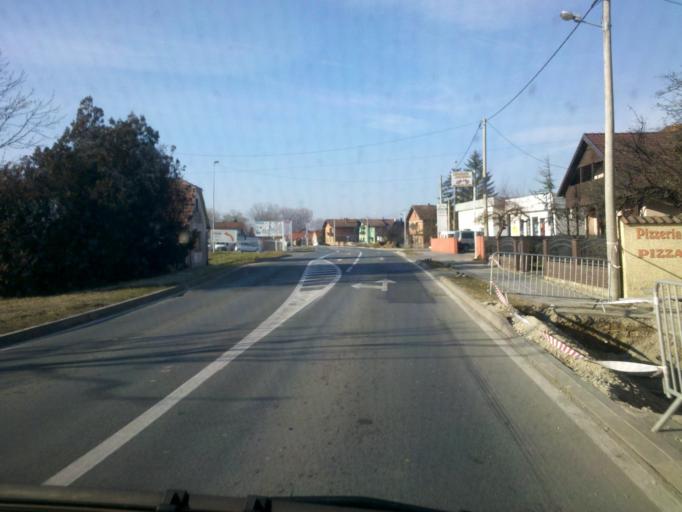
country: HR
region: Koprivnicko-Krizevacka
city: Kalinovac
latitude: 46.0288
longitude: 17.0715
